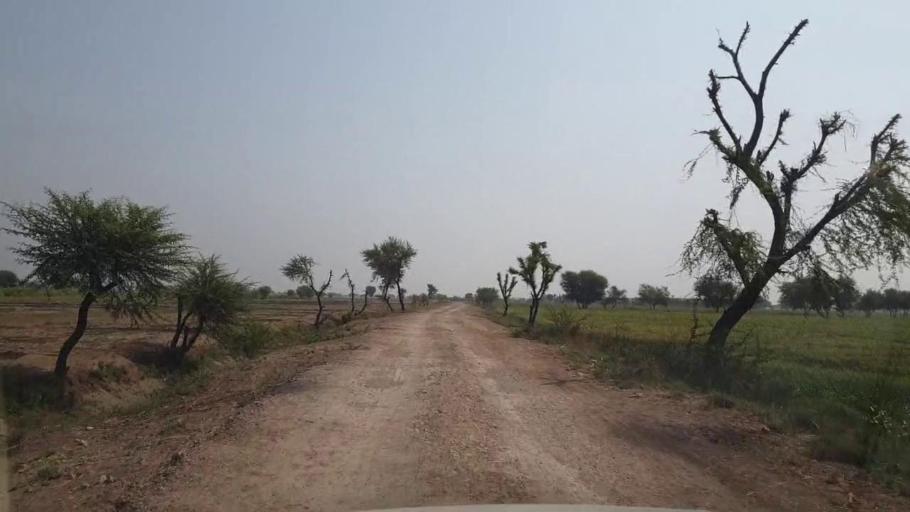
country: PK
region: Sindh
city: Dhoro Naro
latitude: 25.4613
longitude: 69.6633
